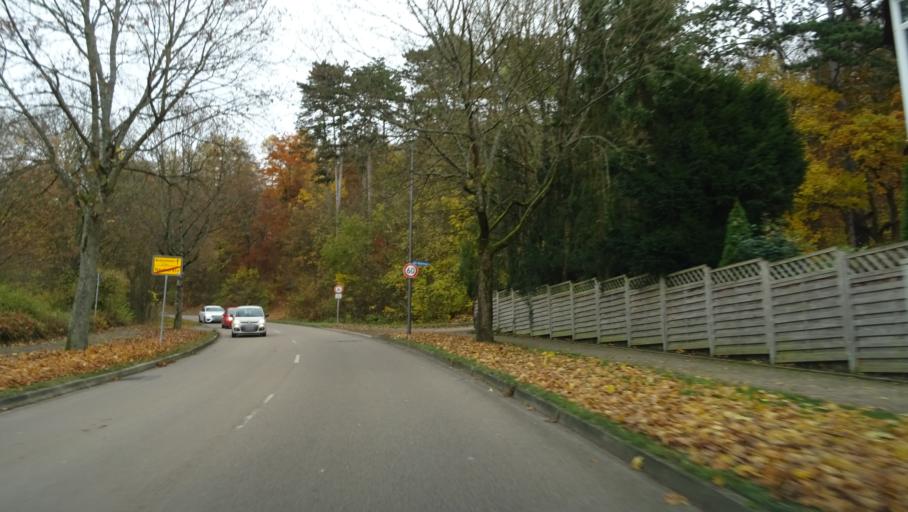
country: DE
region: Baden-Wuerttemberg
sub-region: Karlsruhe Region
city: Neckarzimmern
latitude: 49.3368
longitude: 9.1246
